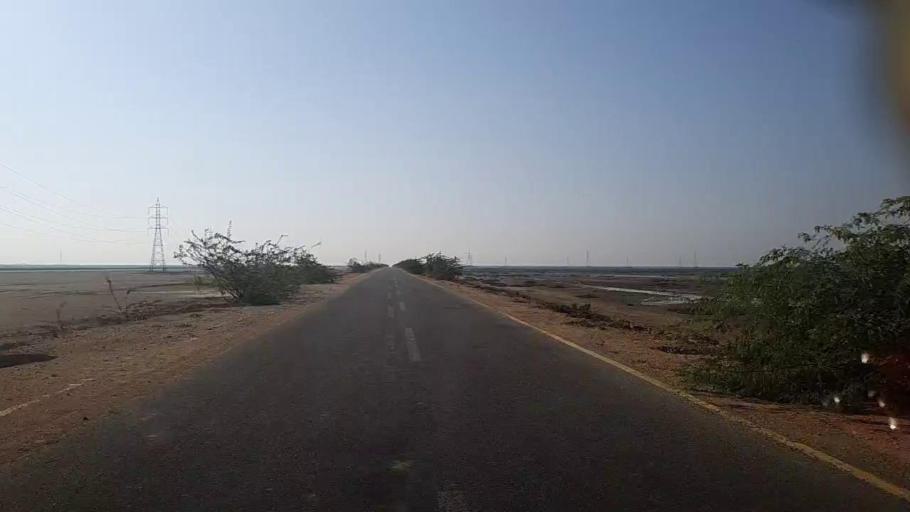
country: PK
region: Sindh
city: Mirpur Sakro
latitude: 24.6009
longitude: 67.4979
